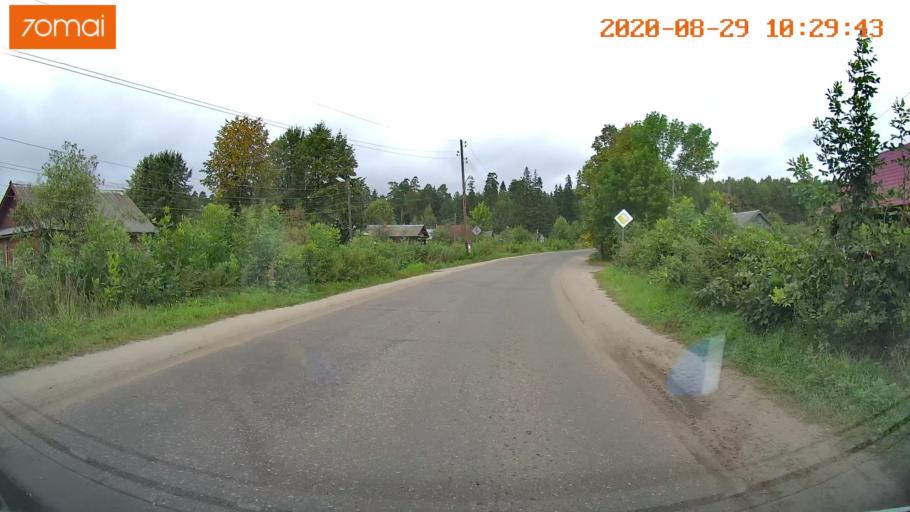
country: RU
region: Ivanovo
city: Yur'yevets
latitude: 57.3121
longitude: 43.0965
